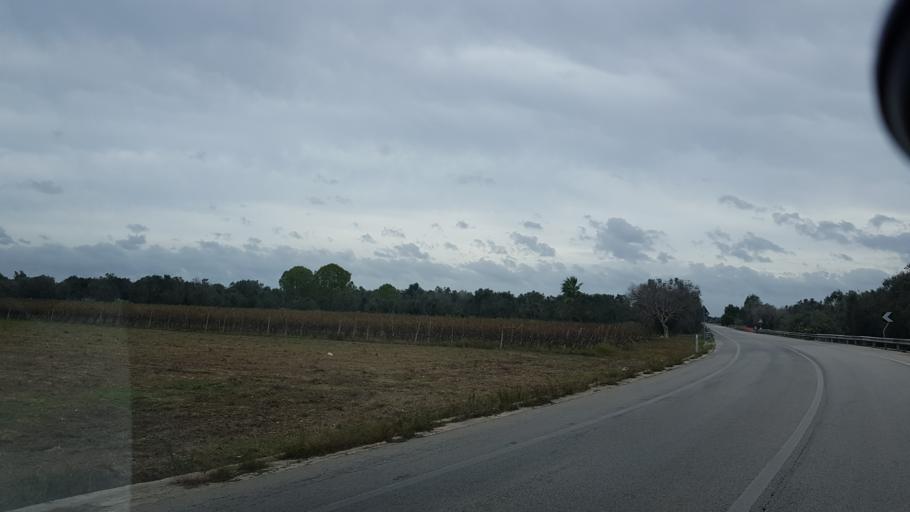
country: IT
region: Apulia
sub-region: Provincia di Lecce
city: Guagnano
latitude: 40.3985
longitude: 17.9226
